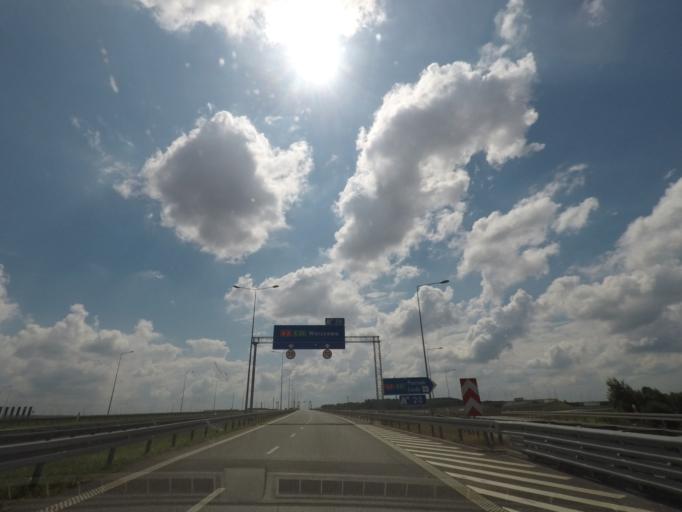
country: PL
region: Lodz Voivodeship
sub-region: Powiat zgierski
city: Strykow
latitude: 51.8949
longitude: 19.6319
